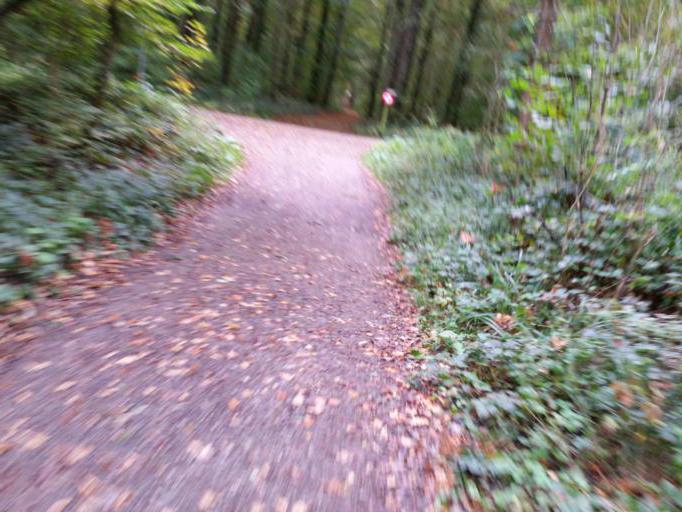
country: CH
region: Thurgau
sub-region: Arbon District
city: Uttwil
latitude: 47.5674
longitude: 9.3450
